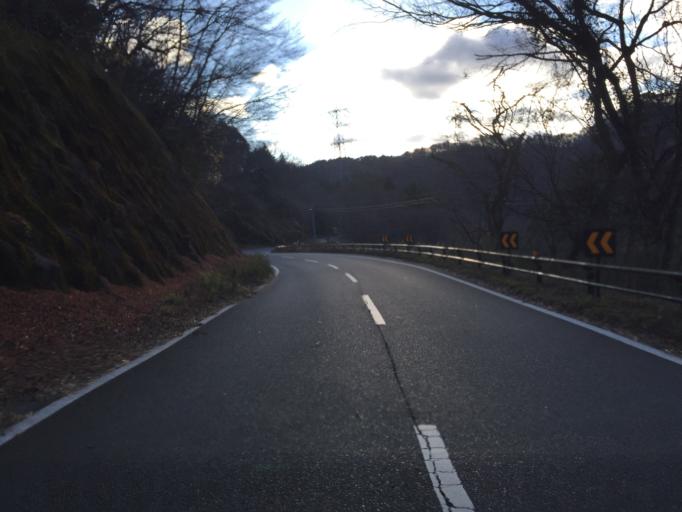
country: JP
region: Fukushima
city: Iwaki
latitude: 37.1613
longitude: 140.8257
